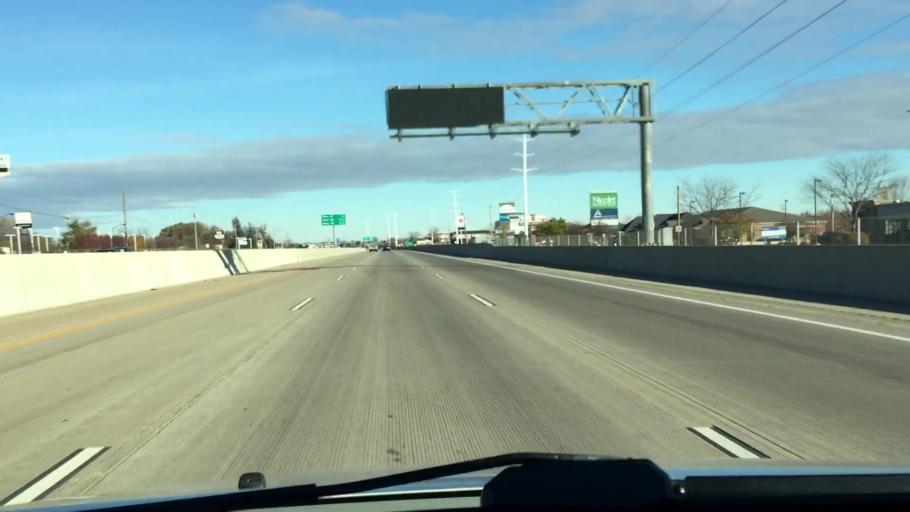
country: US
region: Wisconsin
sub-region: Winnebago County
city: Oshkosh
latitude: 44.0215
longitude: -88.5819
